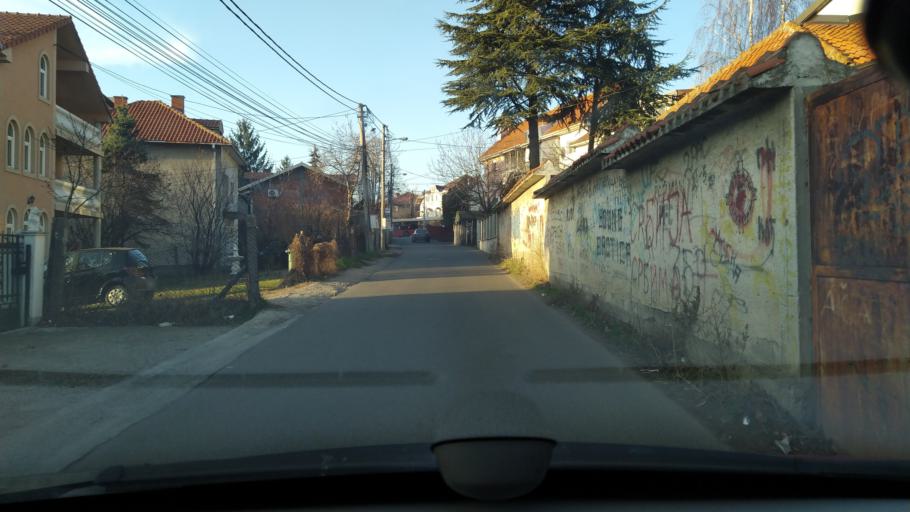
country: RS
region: Central Serbia
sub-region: Belgrade
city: Zvezdara
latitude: 44.7656
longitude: 20.5610
